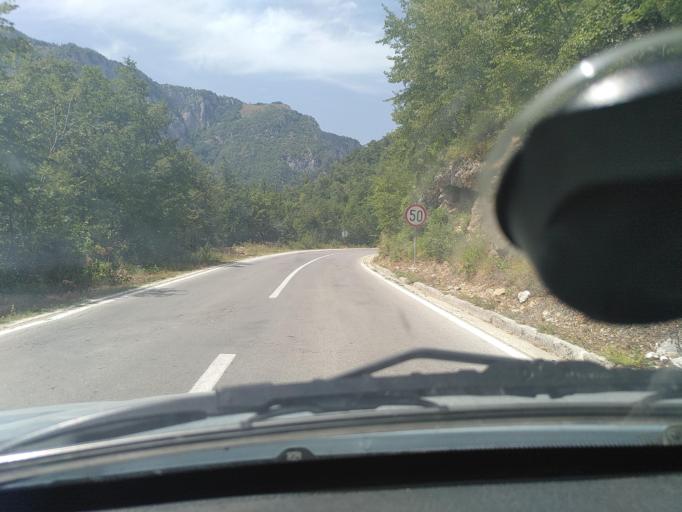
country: ME
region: Opstina Pluzine
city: Pluzine
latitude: 43.2182
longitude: 18.8542
